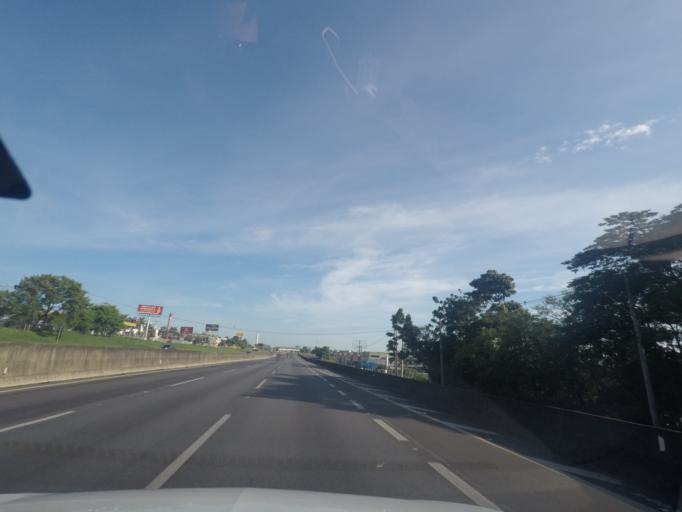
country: BR
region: Sao Paulo
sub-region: Americana
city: Americana
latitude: -22.7261
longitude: -47.2926
